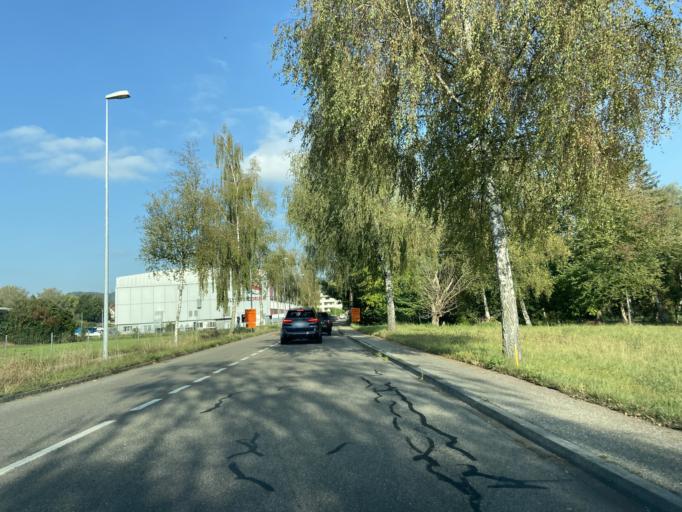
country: CH
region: Zurich
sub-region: Bezirk Pfaeffikon
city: Pfaeffikon / Pfaeffikon (Dorfkern)
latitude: 47.3643
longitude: 8.7701
